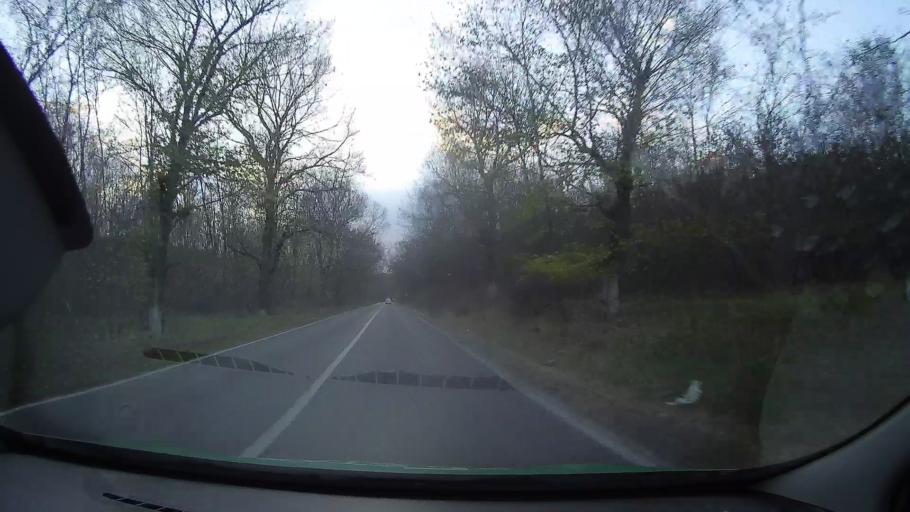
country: RO
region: Constanta
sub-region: Comuna Baneasa
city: Baneasa
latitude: 44.0874
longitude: 27.6632
